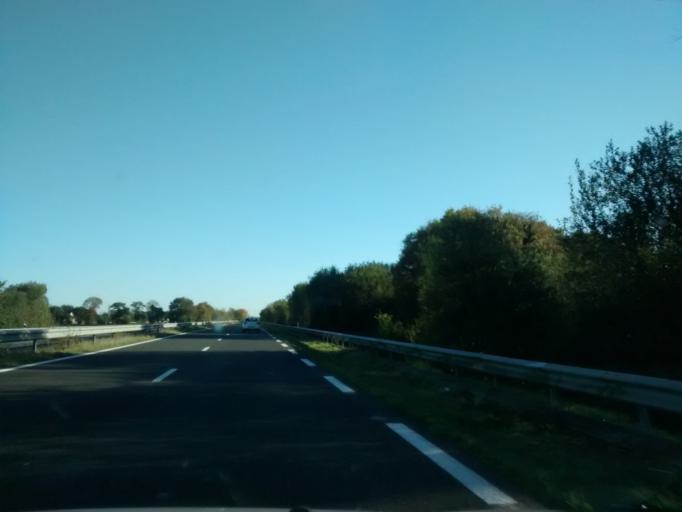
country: FR
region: Brittany
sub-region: Departement des Cotes-d'Armor
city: Cavan
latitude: 48.6648
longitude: -3.3453
